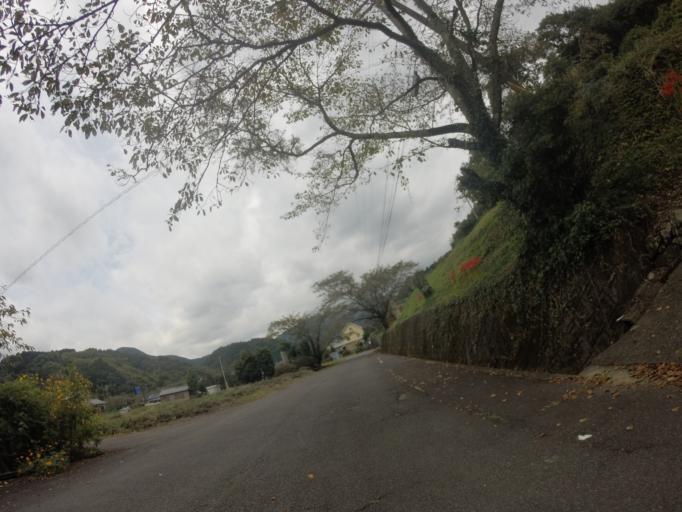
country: JP
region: Shizuoka
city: Fujieda
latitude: 34.9192
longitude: 138.2086
